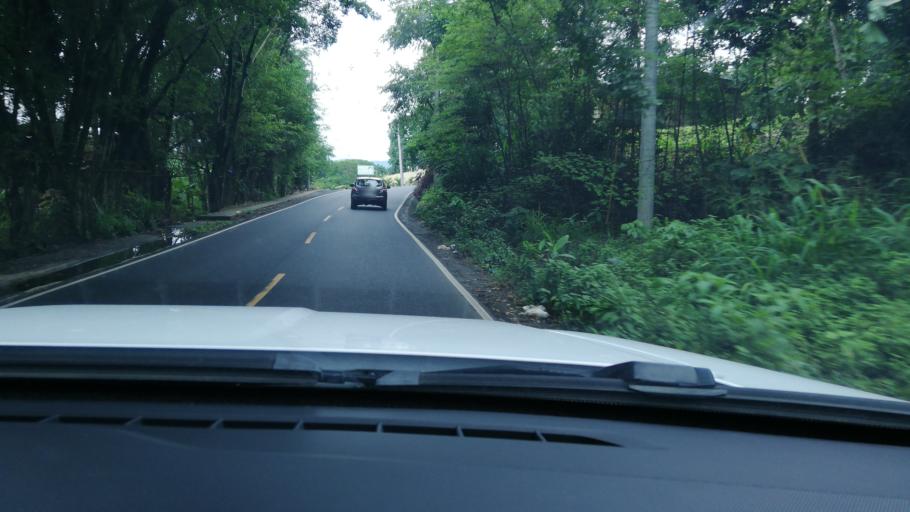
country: PA
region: Panama
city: Las Cumbres
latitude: 9.0735
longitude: -79.5172
